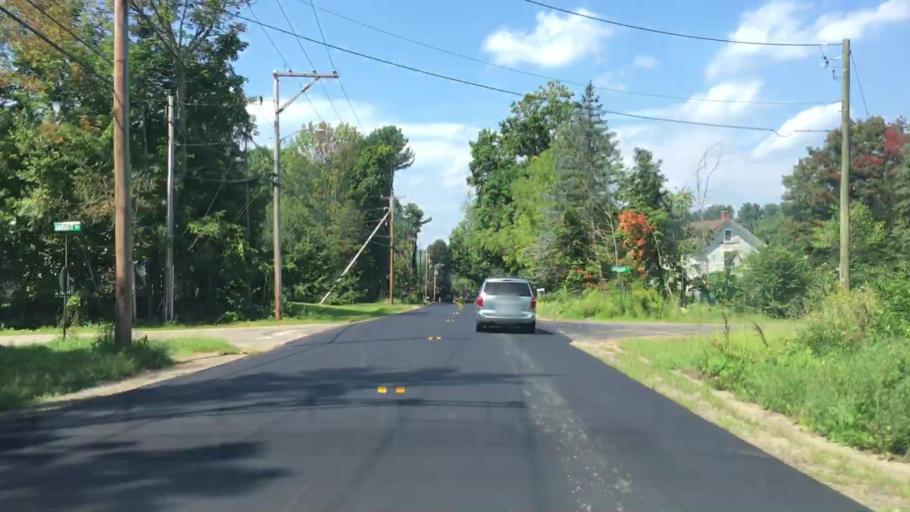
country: US
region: New Hampshire
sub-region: Rockingham County
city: Hampstead
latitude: 42.8942
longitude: -71.2101
